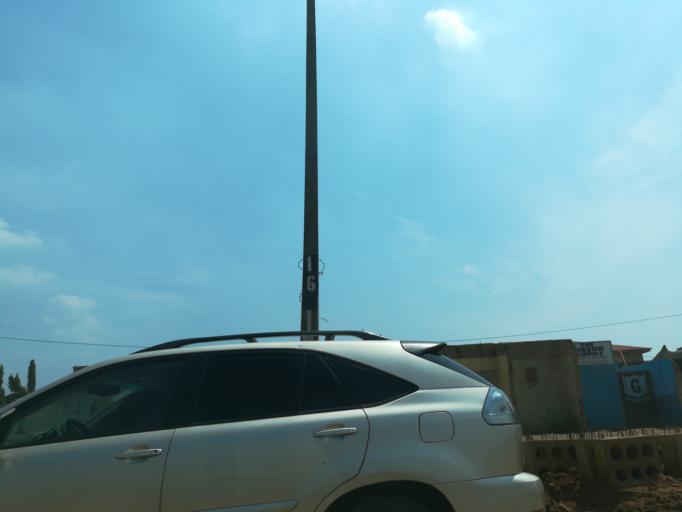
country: NG
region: Lagos
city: Ikorodu
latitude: 6.6462
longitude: 3.4792
